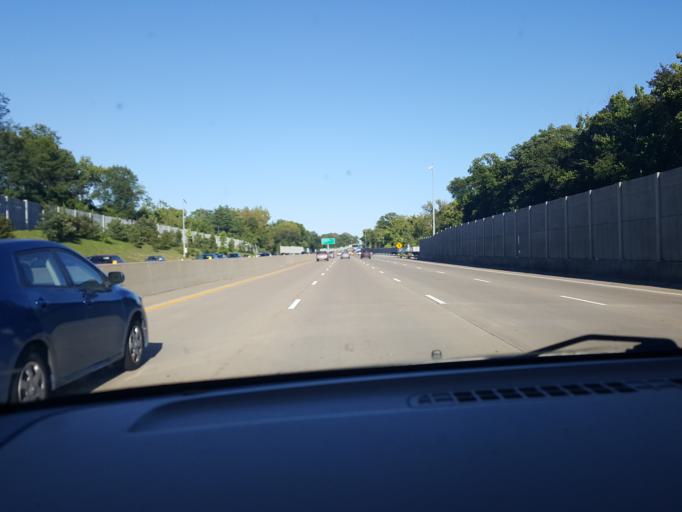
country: US
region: Missouri
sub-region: Saint Louis County
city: Ladue
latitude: 38.6316
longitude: -90.3818
